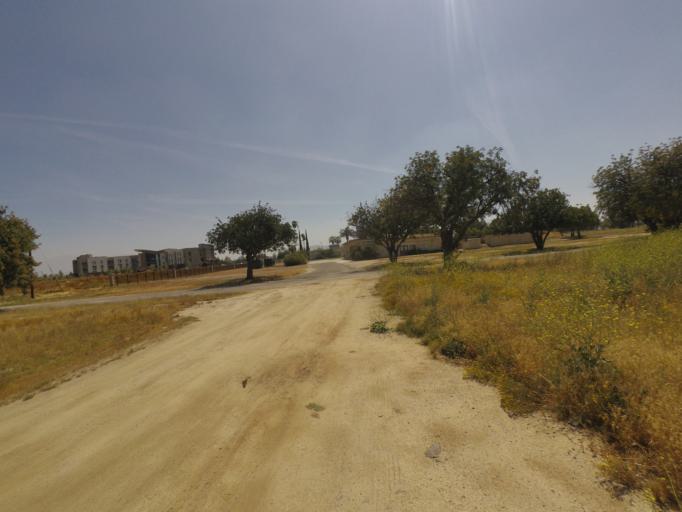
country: US
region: California
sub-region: Riverside County
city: March Air Force Base
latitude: 33.8975
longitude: -117.2499
